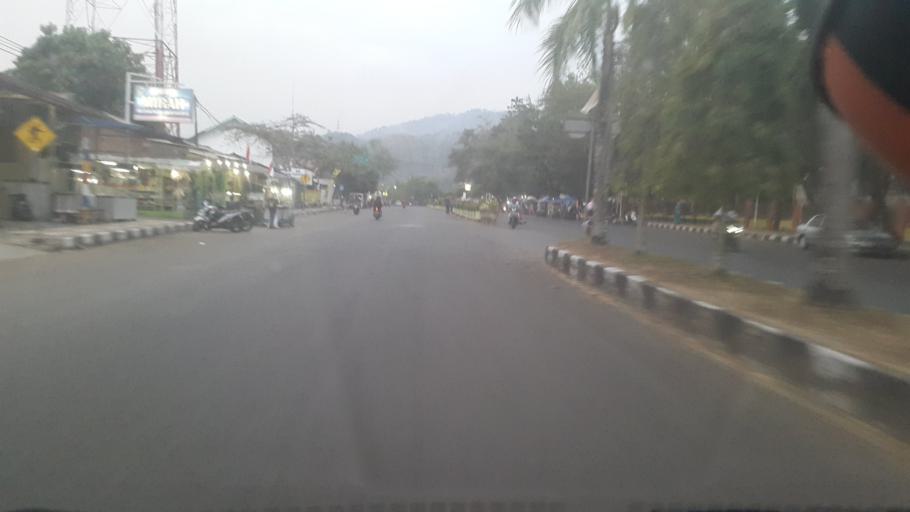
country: ID
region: West Java
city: Pelabuhanratu
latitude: -6.9891
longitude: 106.5570
